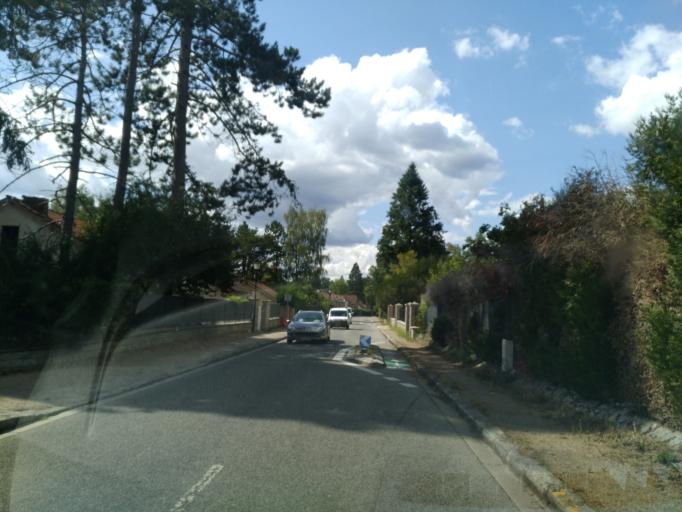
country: FR
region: Ile-de-France
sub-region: Departement des Yvelines
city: Saint-Arnoult-en-Yvelines
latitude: 48.6104
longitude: 1.9166
